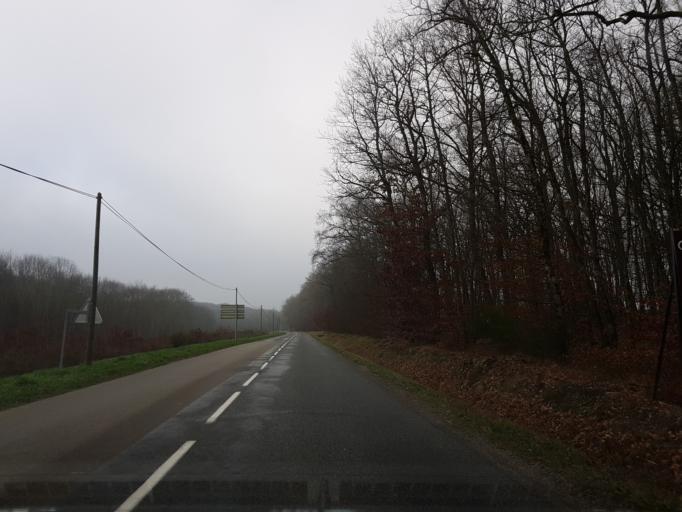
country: FR
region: Bourgogne
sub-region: Departement de Saone-et-Loire
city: Toulon-sur-Arroux
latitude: 46.6858
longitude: 4.1735
